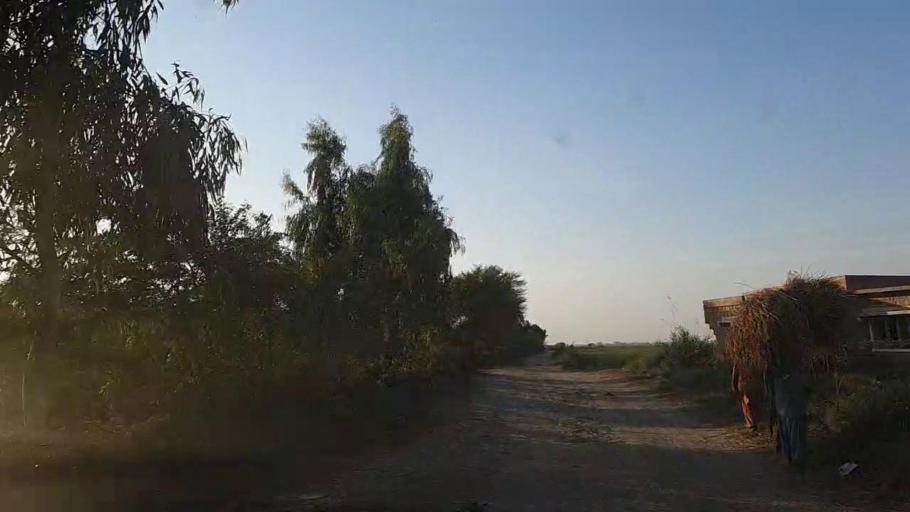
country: PK
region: Sindh
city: Mirpur Batoro
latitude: 24.6821
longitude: 68.2132
